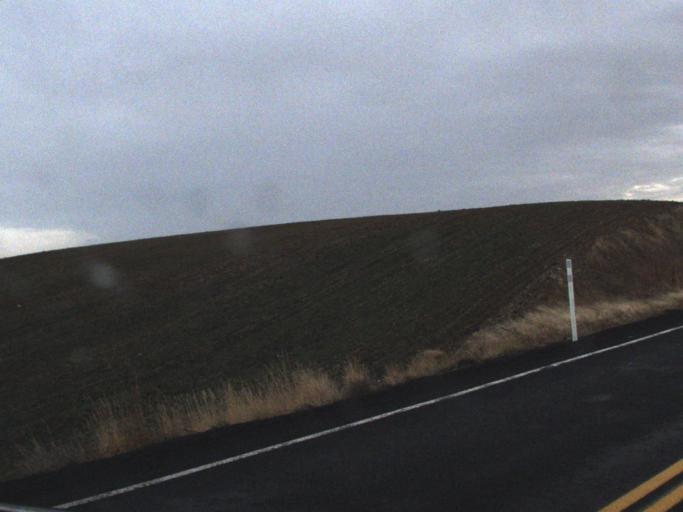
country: US
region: Washington
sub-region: Lincoln County
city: Davenport
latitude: 47.7238
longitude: -118.1532
